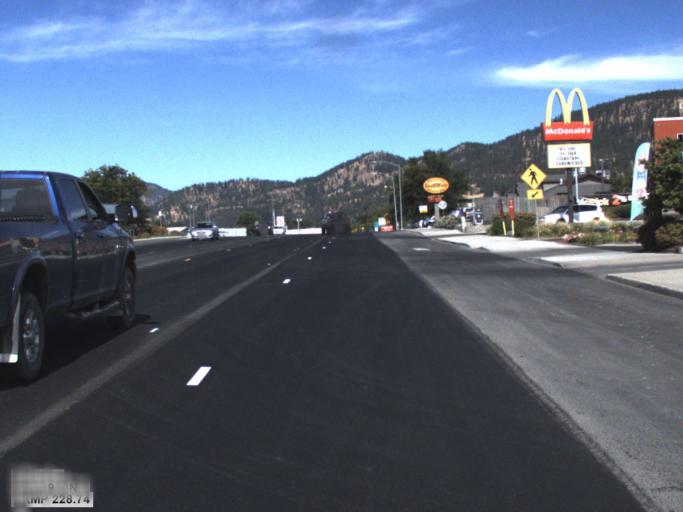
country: US
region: Washington
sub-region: Stevens County
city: Colville
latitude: 48.5336
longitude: -117.9048
